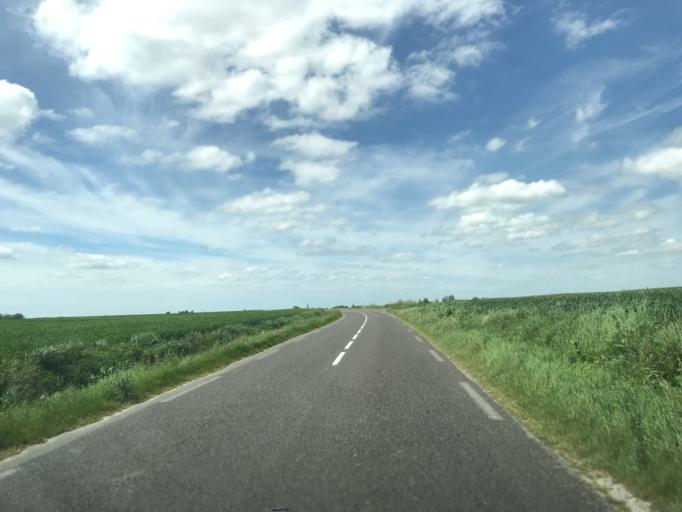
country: FR
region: Haute-Normandie
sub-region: Departement de l'Eure
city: Nassandres
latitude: 49.1595
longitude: 0.8040
